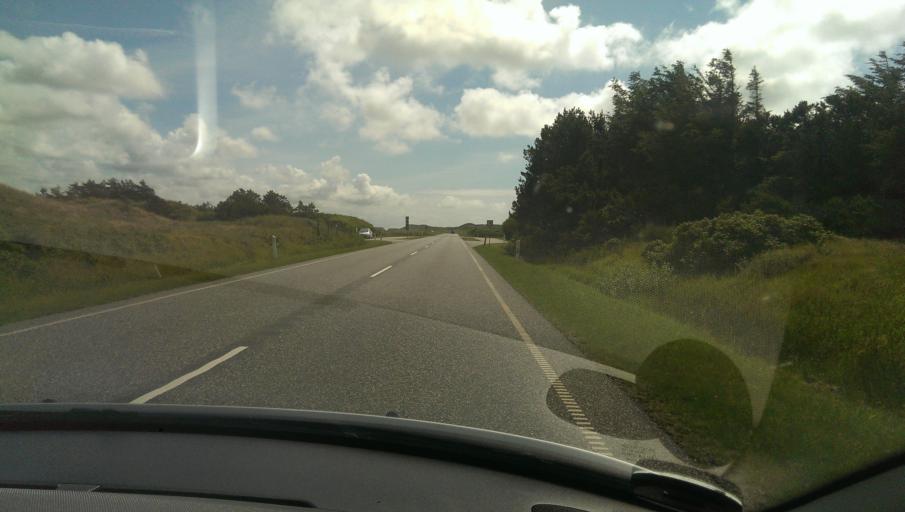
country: DK
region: Central Jutland
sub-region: Holstebro Kommune
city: Ulfborg
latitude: 56.2429
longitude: 8.1393
